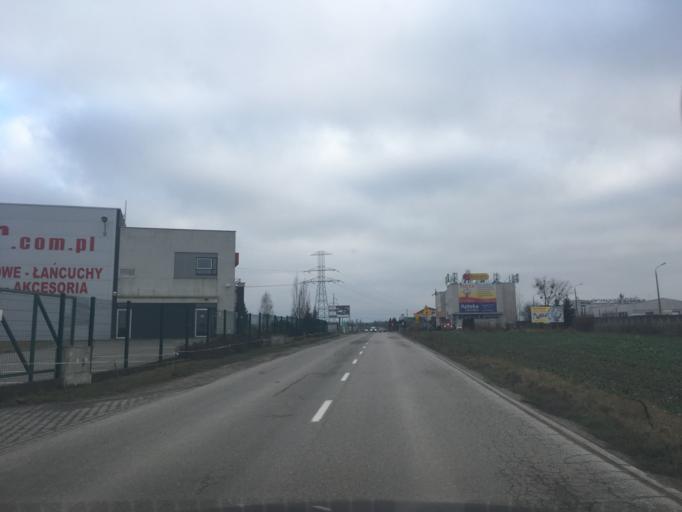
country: PL
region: Masovian Voivodeship
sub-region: Powiat piaseczynski
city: Lesznowola
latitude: 52.0834
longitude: 20.9684
